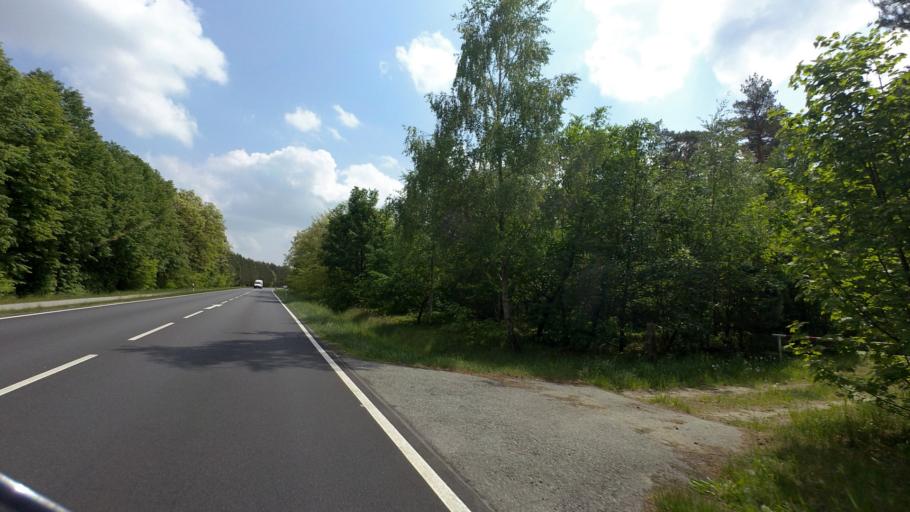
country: DE
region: Saxony
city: Niesky
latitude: 51.3222
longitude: 14.8239
